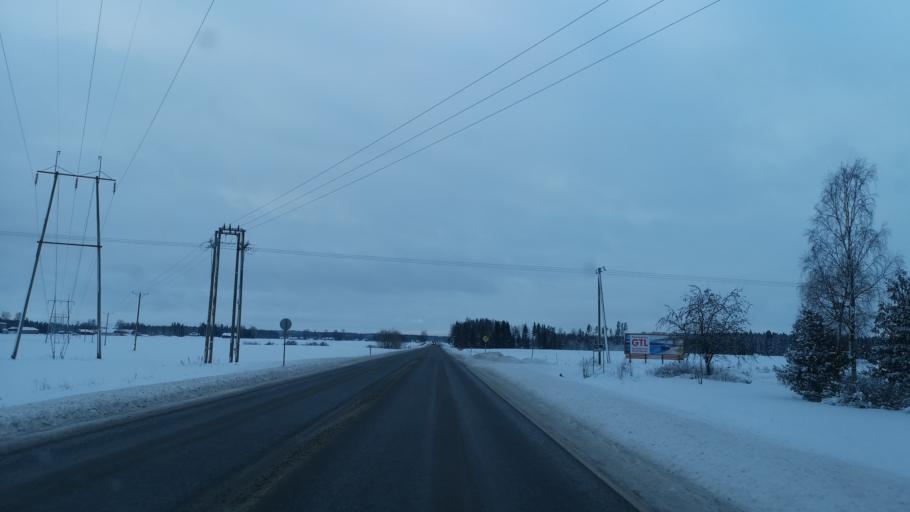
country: FI
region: Varsinais-Suomi
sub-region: Loimaa
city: Loimaa
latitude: 60.8958
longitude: 23.1218
